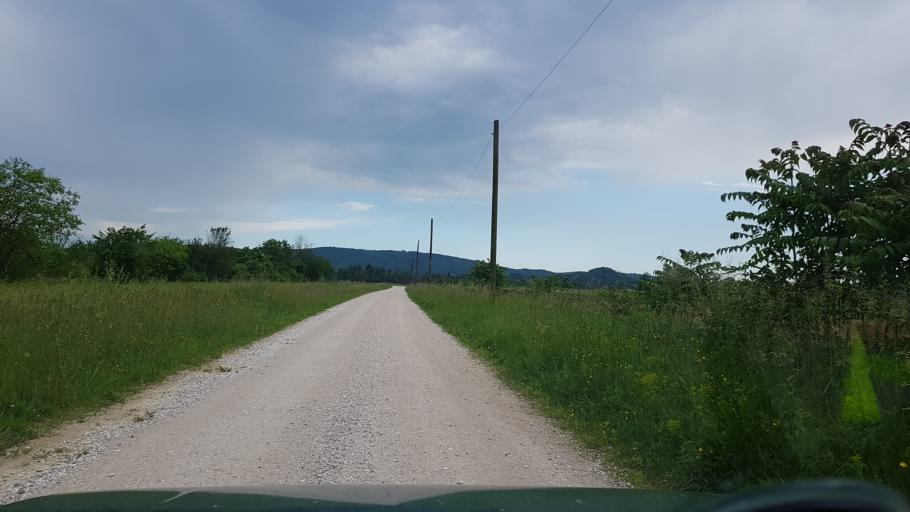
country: IT
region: Friuli Venezia Giulia
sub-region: Provincia di Gorizia
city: Mossa
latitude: 45.9283
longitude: 13.5426
